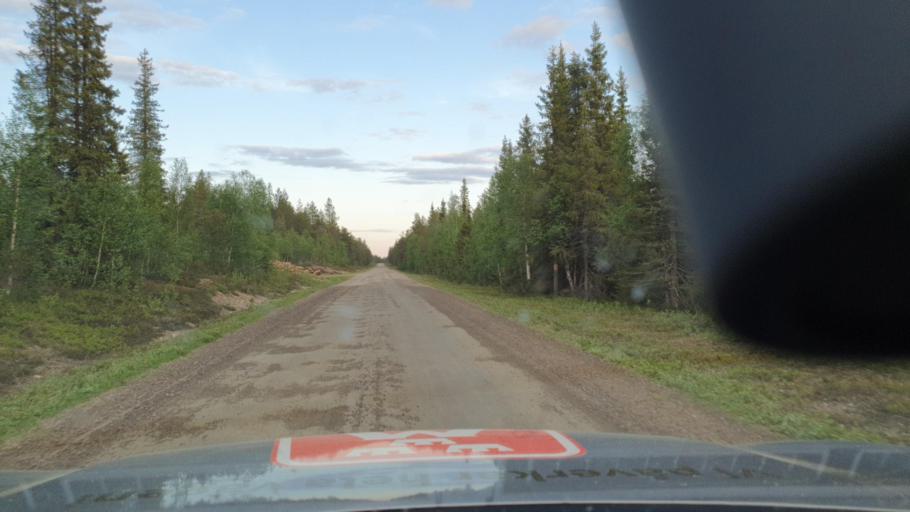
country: SE
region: Norrbotten
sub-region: Bodens Kommun
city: Boden
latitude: 66.5816
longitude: 21.4028
